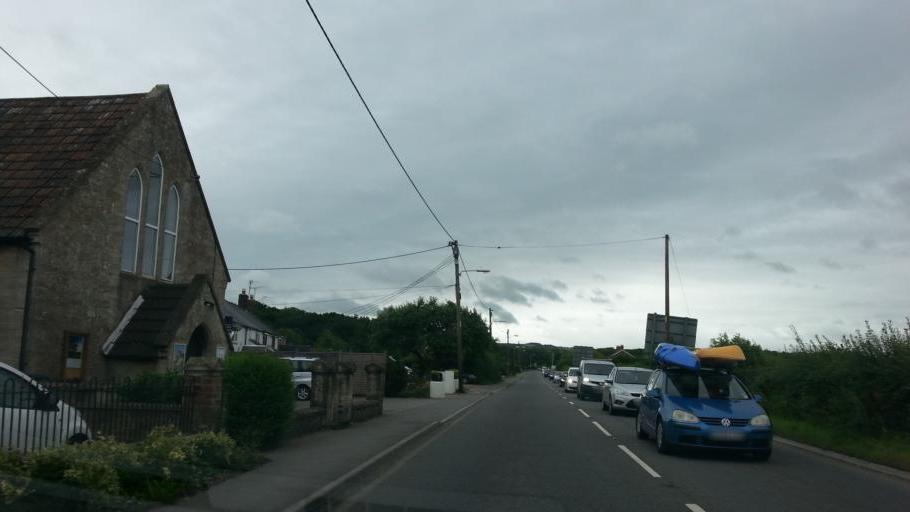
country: GB
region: England
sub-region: Wiltshire
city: North Bradley
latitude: 51.2932
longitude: -2.1903
